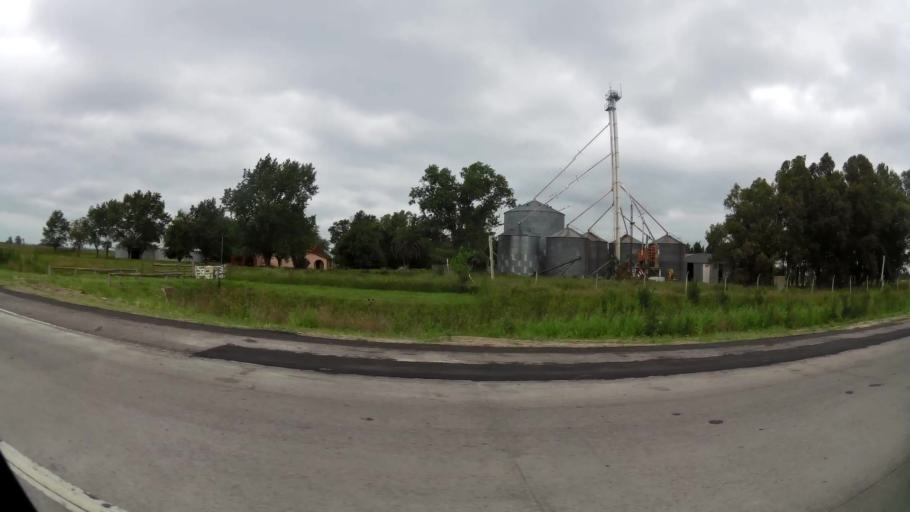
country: AR
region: Buenos Aires
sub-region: Partido de San Vicente
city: San Vicente
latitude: -35.0393
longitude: -58.4014
